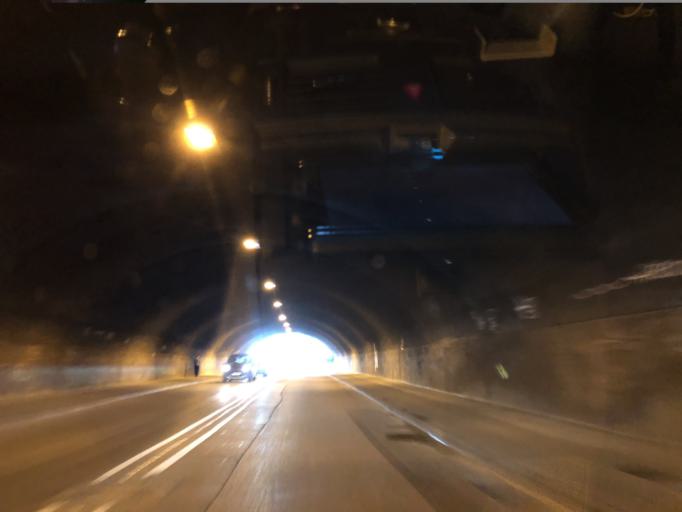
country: DE
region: North Rhine-Westphalia
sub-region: Regierungsbezirk Dusseldorf
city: Essen
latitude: 51.4565
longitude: 7.0341
